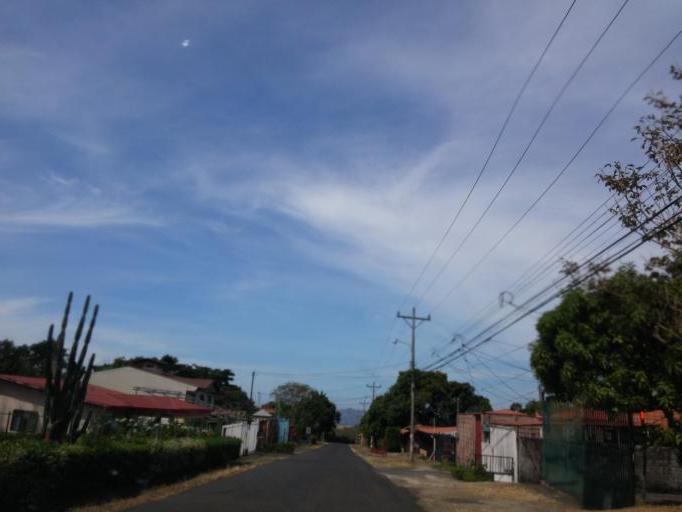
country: CR
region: Alajuela
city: Alajuela
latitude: 10.0438
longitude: -84.2316
